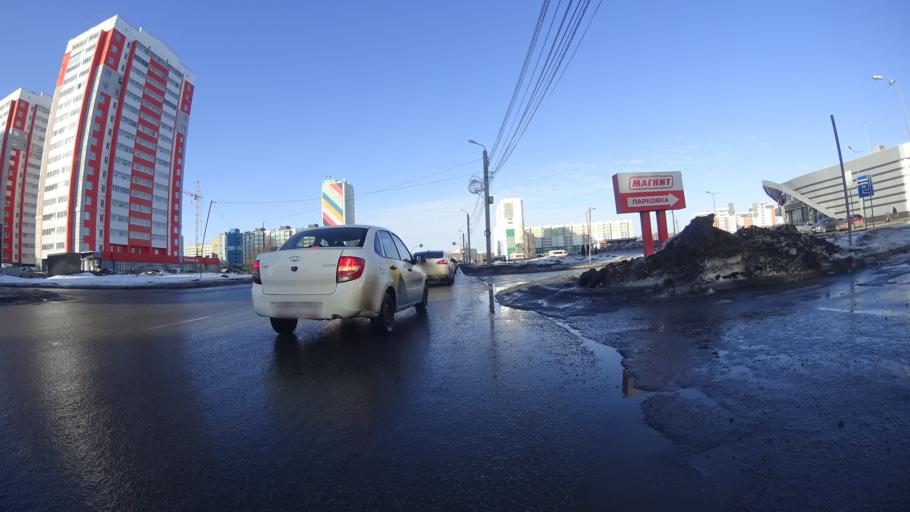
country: RU
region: Chelyabinsk
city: Roshchino
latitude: 55.2088
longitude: 61.2844
